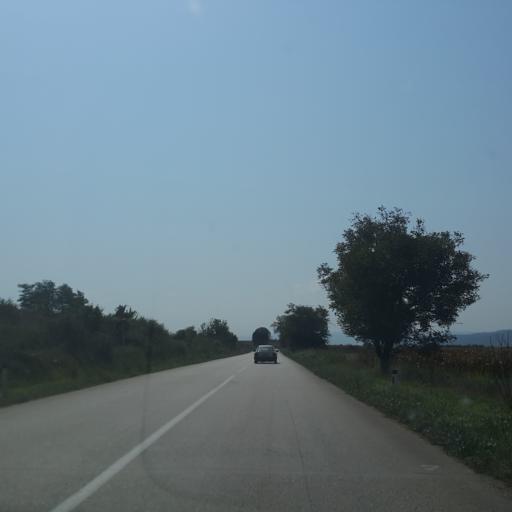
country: RS
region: Central Serbia
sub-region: Zajecarski Okrug
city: Knjazevac
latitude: 43.6770
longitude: 22.2893
